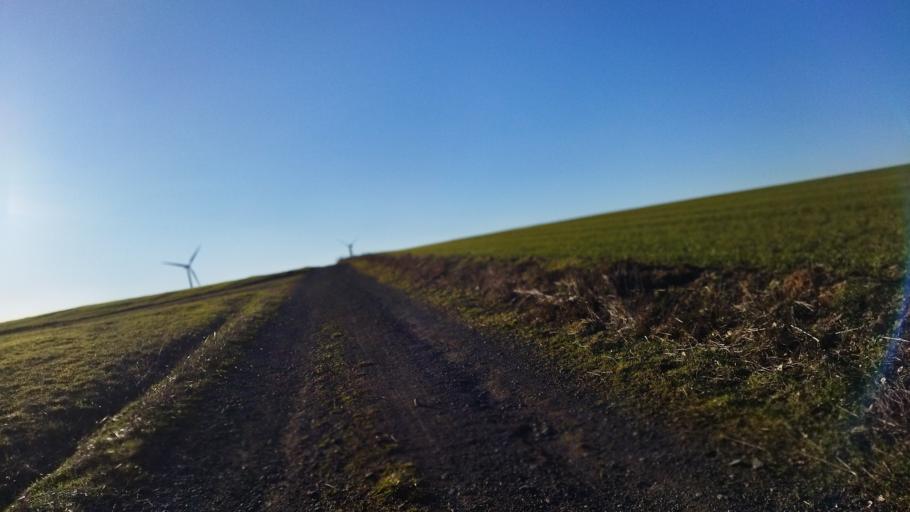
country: DE
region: Rheinland-Pfalz
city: Frohnhofen
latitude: 49.4720
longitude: 7.3006
